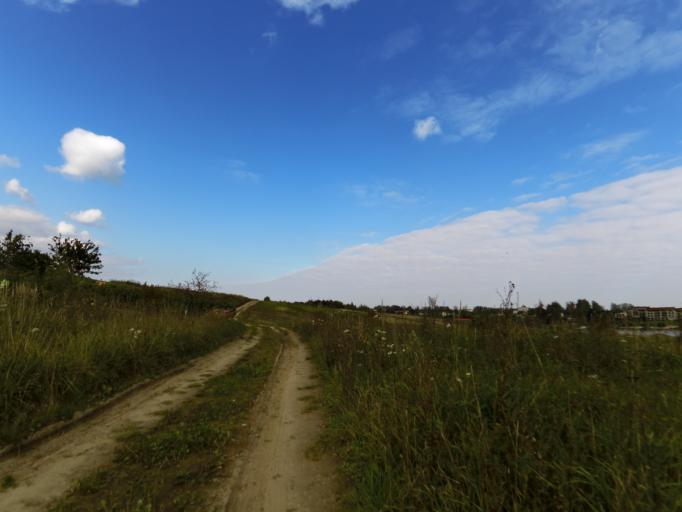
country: LT
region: Vilnius County
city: Pilaite
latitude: 54.7032
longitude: 25.1538
